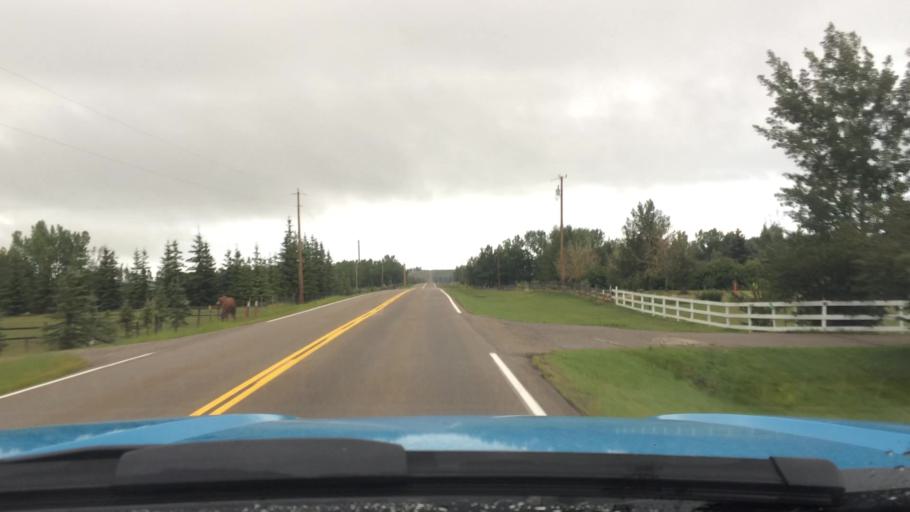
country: CA
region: Alberta
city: Airdrie
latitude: 51.2025
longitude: -114.1411
